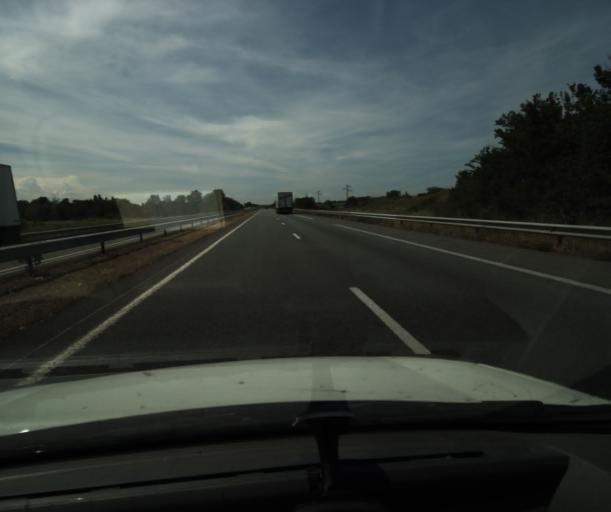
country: FR
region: Languedoc-Roussillon
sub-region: Departement de l'Aude
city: Arzens
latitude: 43.2206
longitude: 2.2072
